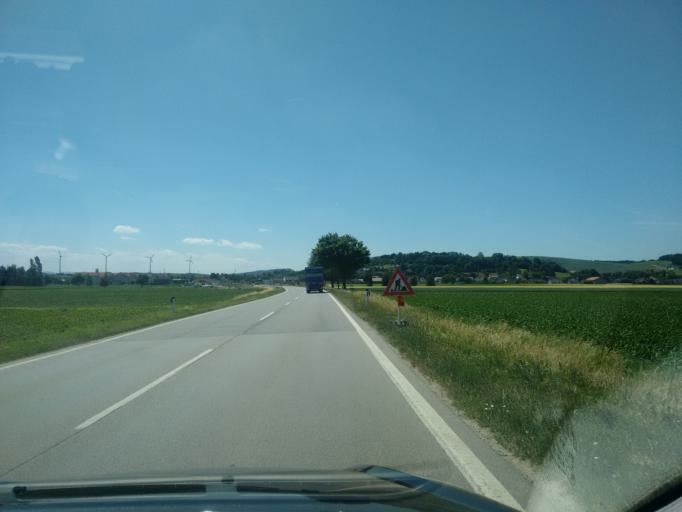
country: AT
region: Lower Austria
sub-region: Politischer Bezirk Sankt Polten
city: Haunoldstein
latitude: 48.1976
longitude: 15.4693
